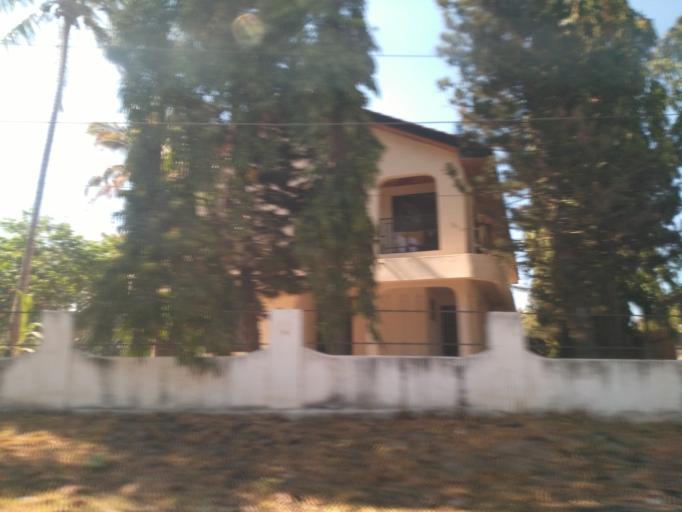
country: TZ
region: Dodoma
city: Dodoma
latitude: -6.1679
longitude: 35.7517
